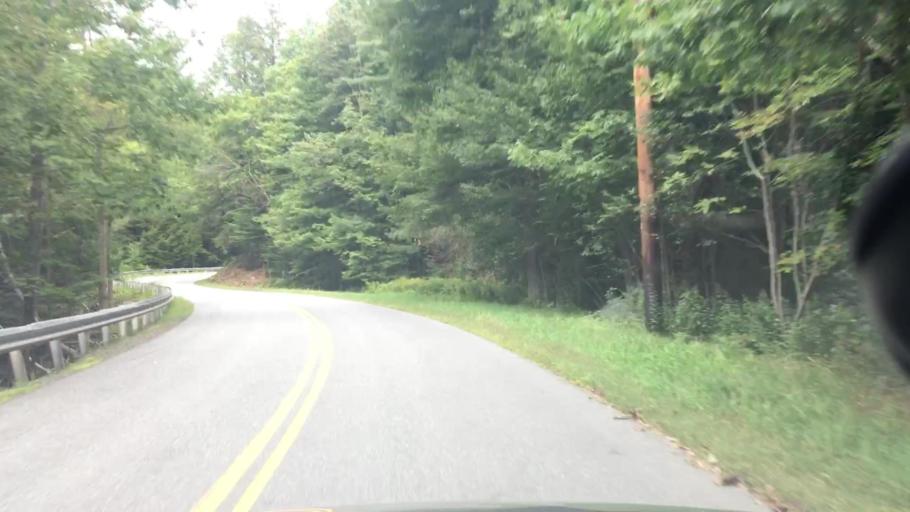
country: US
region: Massachusetts
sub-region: Franklin County
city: Colrain
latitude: 42.7951
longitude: -72.7675
